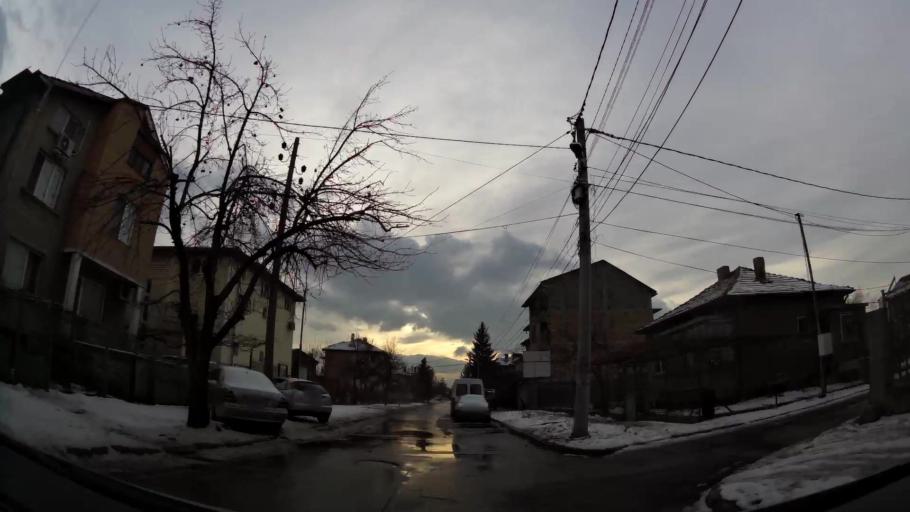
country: BG
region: Sofia-Capital
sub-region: Stolichna Obshtina
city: Sofia
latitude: 42.7263
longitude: 23.3379
